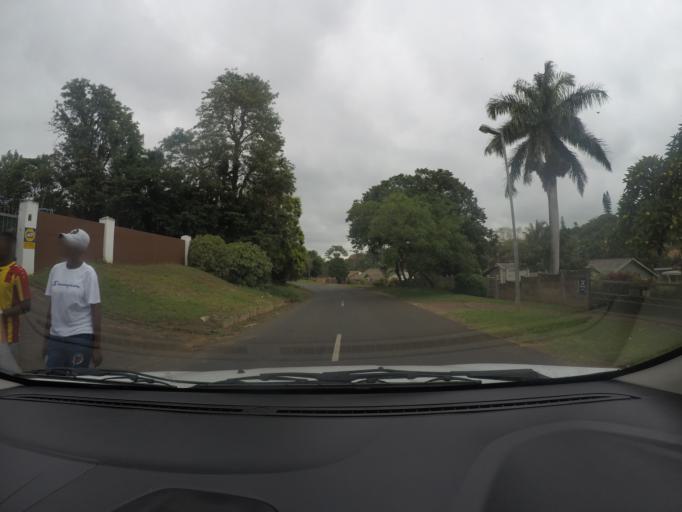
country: ZA
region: KwaZulu-Natal
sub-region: uThungulu District Municipality
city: Empangeni
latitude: -28.7613
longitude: 31.8903
